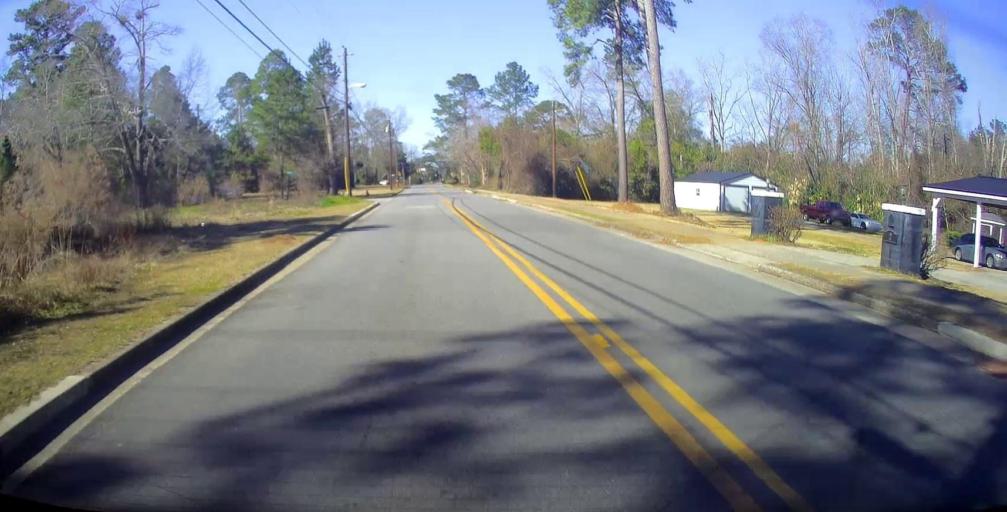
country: US
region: Georgia
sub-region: Macon County
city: Montezuma
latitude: 32.2914
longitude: -84.0306
